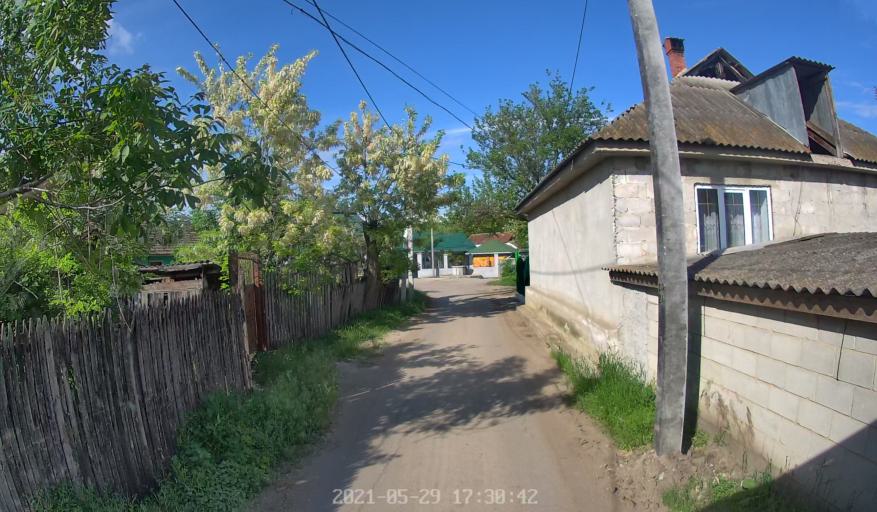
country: MD
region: Laloveni
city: Ialoveni
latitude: 46.8358
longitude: 28.8451
